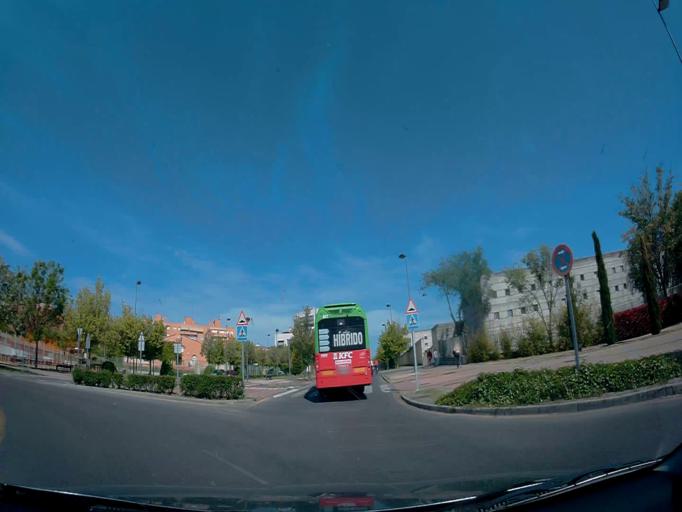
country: ES
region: Madrid
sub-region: Provincia de Madrid
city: Alcorcon
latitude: 40.3462
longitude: -3.8377
